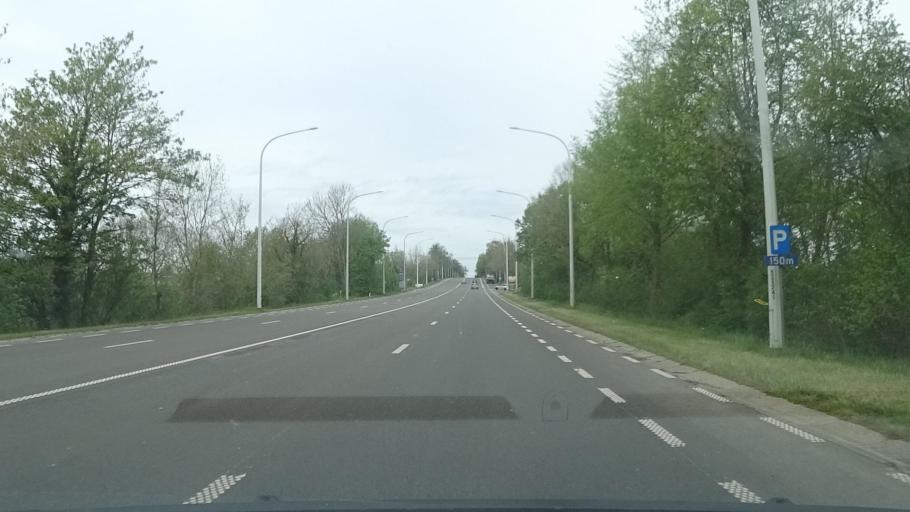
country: BE
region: Wallonia
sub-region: Province de Namur
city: Floreffe
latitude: 50.5013
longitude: 4.7820
